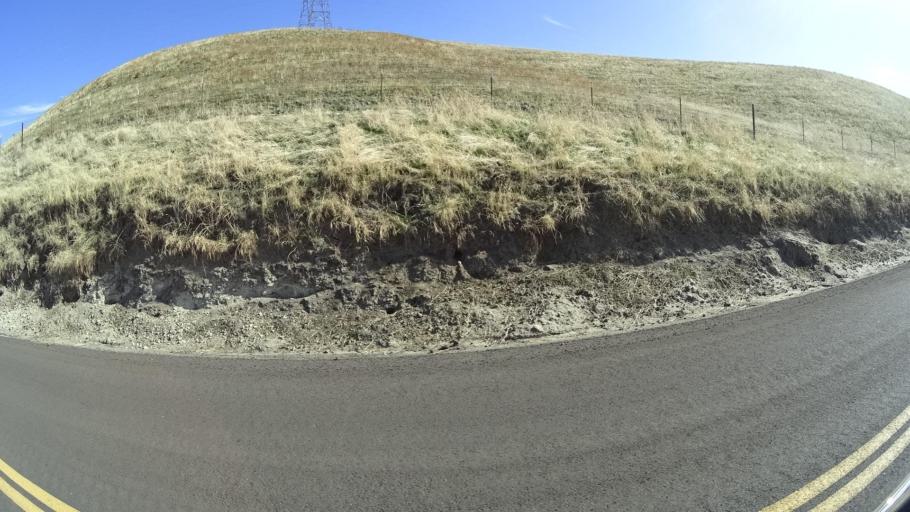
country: US
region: California
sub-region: Tulare County
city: Richgrove
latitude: 35.6616
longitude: -118.9210
